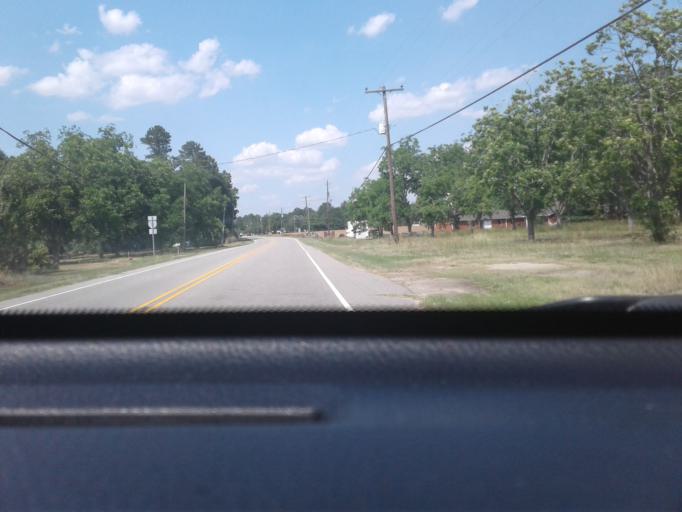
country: US
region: North Carolina
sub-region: Cumberland County
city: Eastover
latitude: 35.1616
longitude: -78.7288
